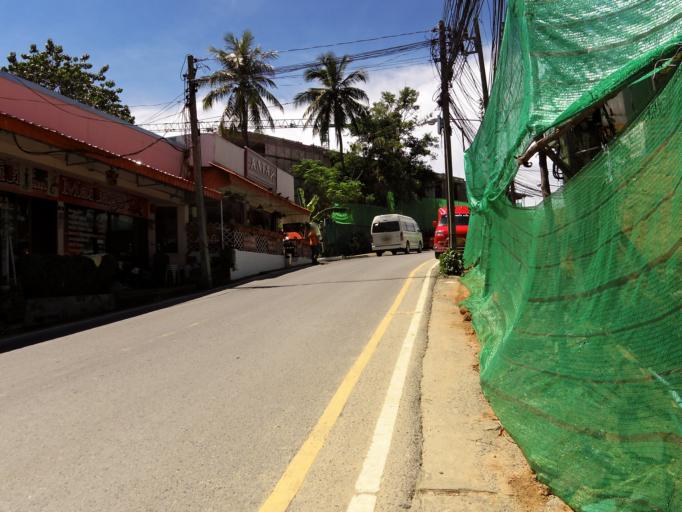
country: TH
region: Phuket
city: Ban Karon
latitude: 7.8256
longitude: 98.2966
